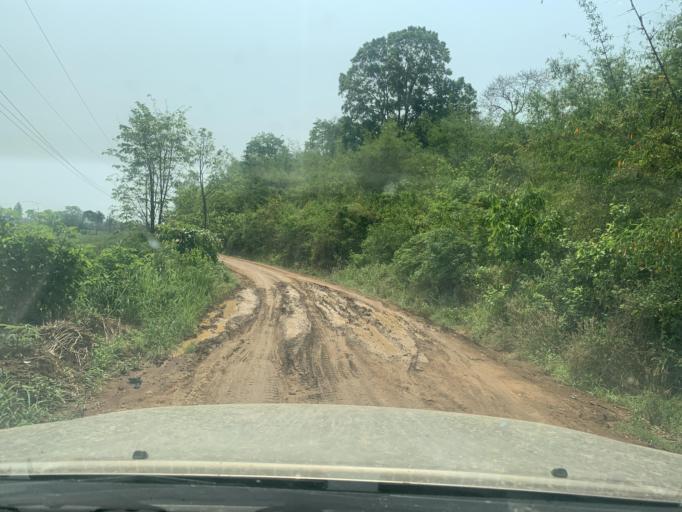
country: TH
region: Uttaradit
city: Ban Khok
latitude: 18.3602
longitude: 101.3856
